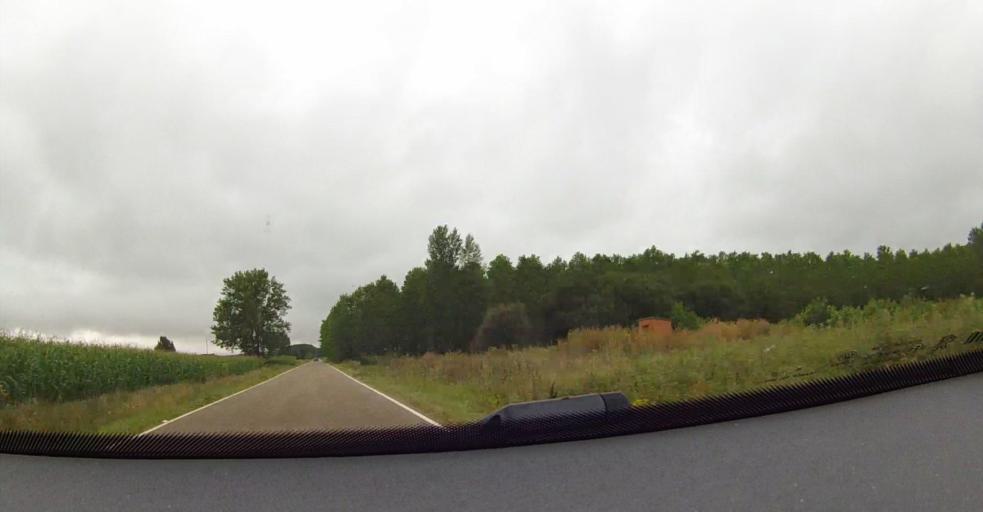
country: ES
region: Castille and Leon
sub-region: Provincia de Palencia
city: Pedrosa de la Vega
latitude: 42.4830
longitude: -4.7243
